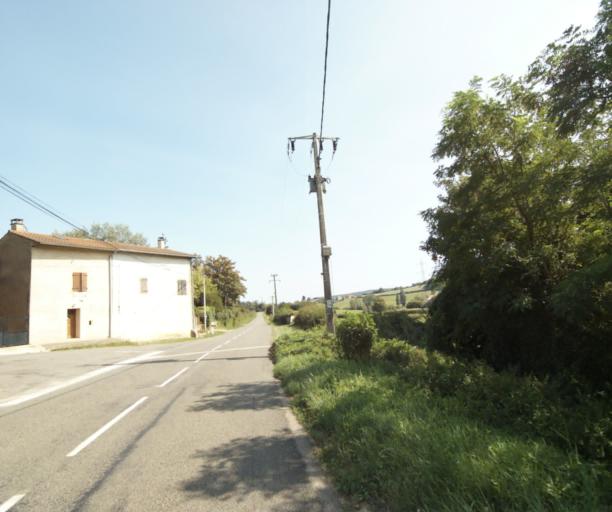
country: FR
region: Bourgogne
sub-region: Departement de Saone-et-Loire
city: Tournus
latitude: 46.5655
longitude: 4.8823
